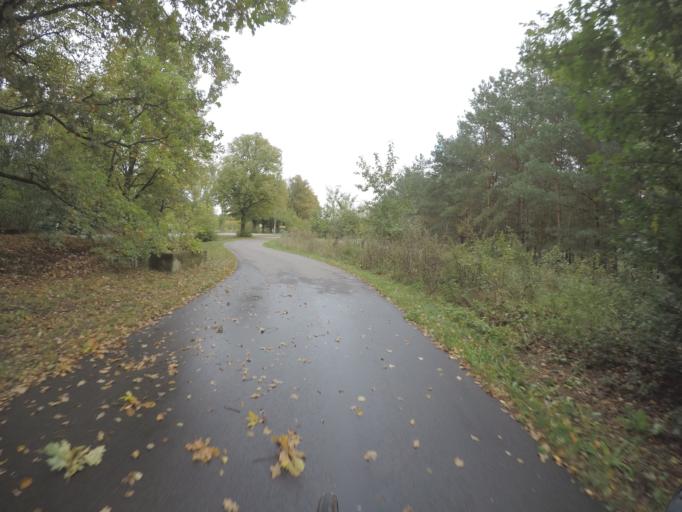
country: DE
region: Berlin
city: Buch
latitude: 52.6597
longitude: 13.4912
